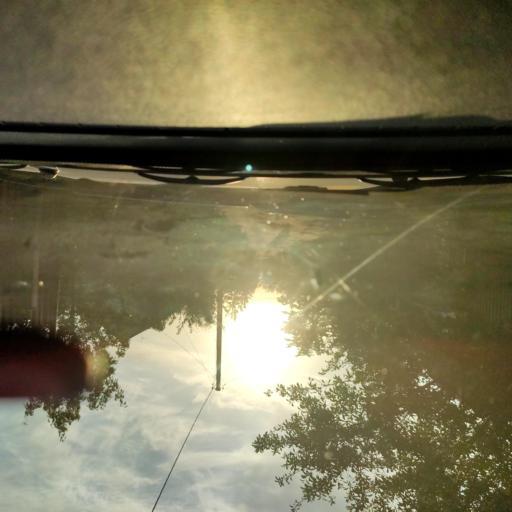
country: RU
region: Voronezj
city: Podgornoye
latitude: 51.8354
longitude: 39.1896
